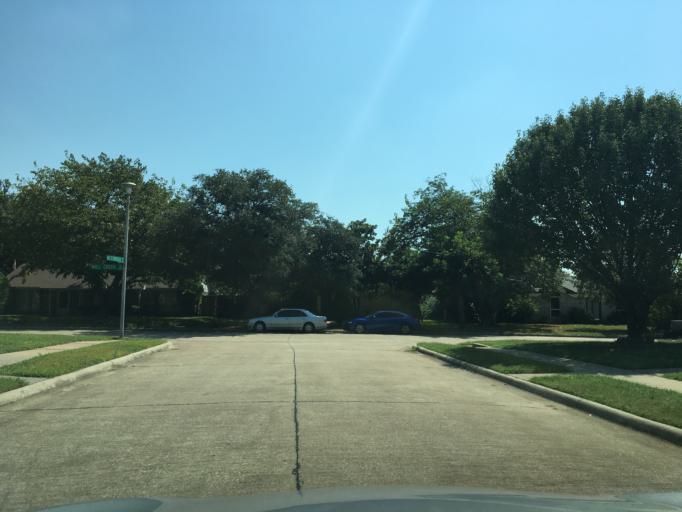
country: US
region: Texas
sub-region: Dallas County
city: Garland
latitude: 32.9322
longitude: -96.6532
